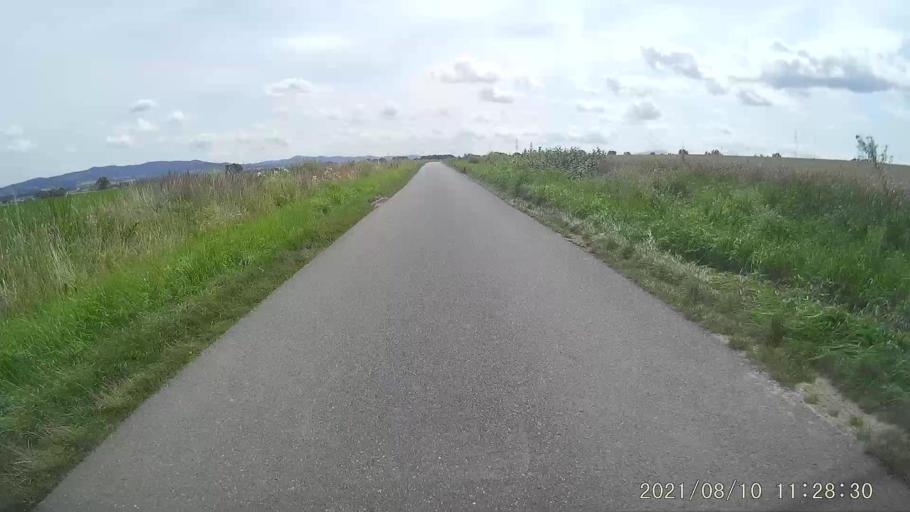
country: PL
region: Lower Silesian Voivodeship
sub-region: Powiat klodzki
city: Polanica-Zdroj
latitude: 50.4399
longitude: 16.5750
